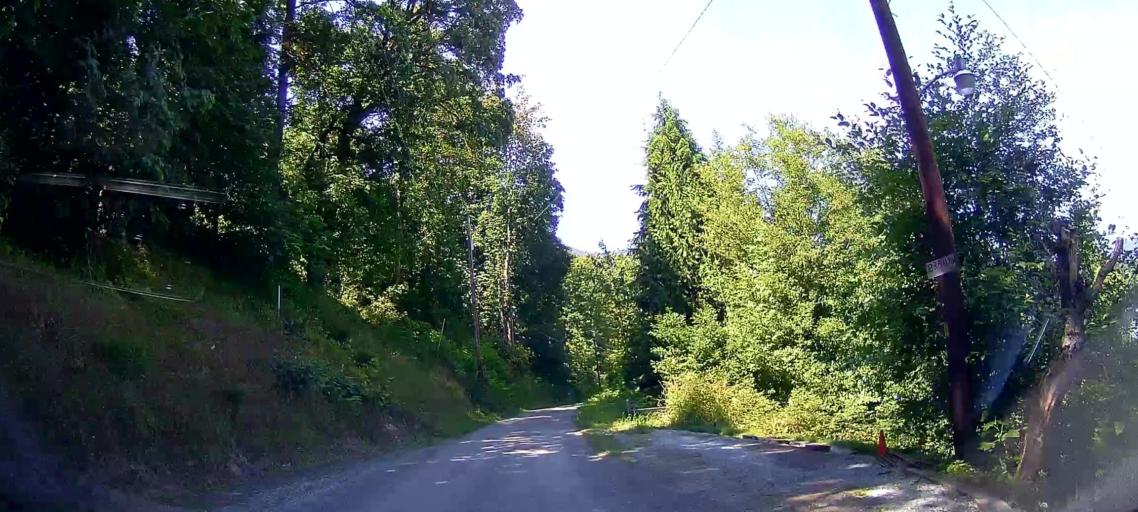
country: US
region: Washington
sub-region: Whatcom County
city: Sudden Valley
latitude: 48.6502
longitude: -122.3333
